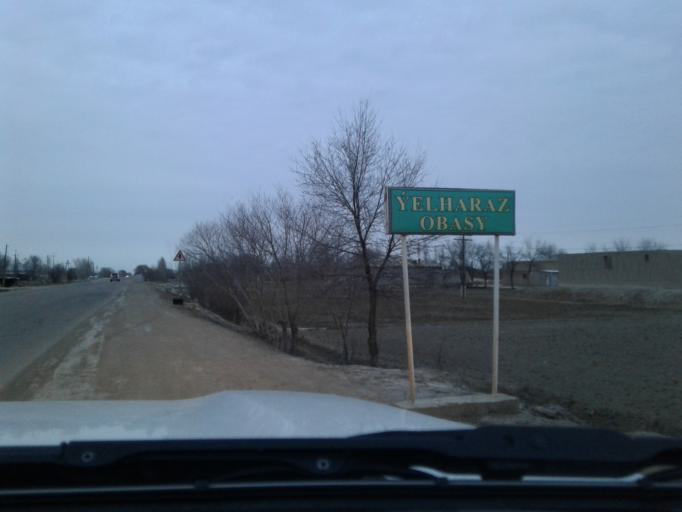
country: UZ
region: Karakalpakstan
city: Manghit
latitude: 42.0364
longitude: 59.9172
